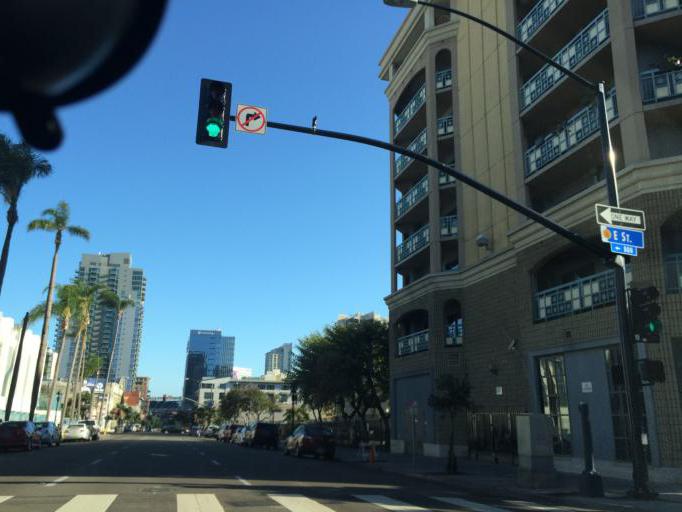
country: US
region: California
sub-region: San Diego County
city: San Diego
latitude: 32.7147
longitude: -117.1574
